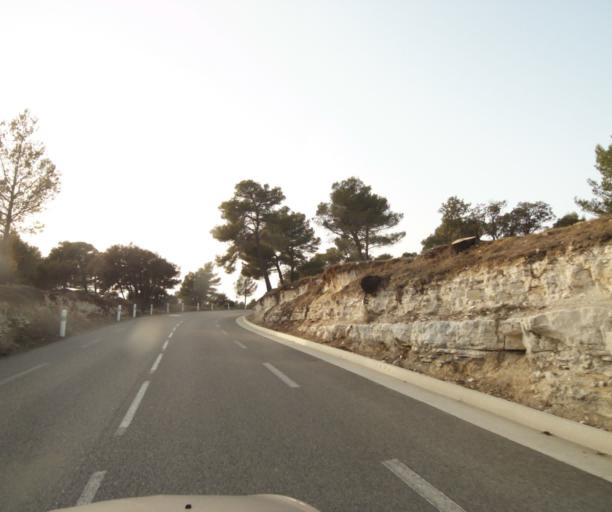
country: FR
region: Provence-Alpes-Cote d'Azur
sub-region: Departement des Bouches-du-Rhone
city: Rognes
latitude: 43.6240
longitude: 5.3503
